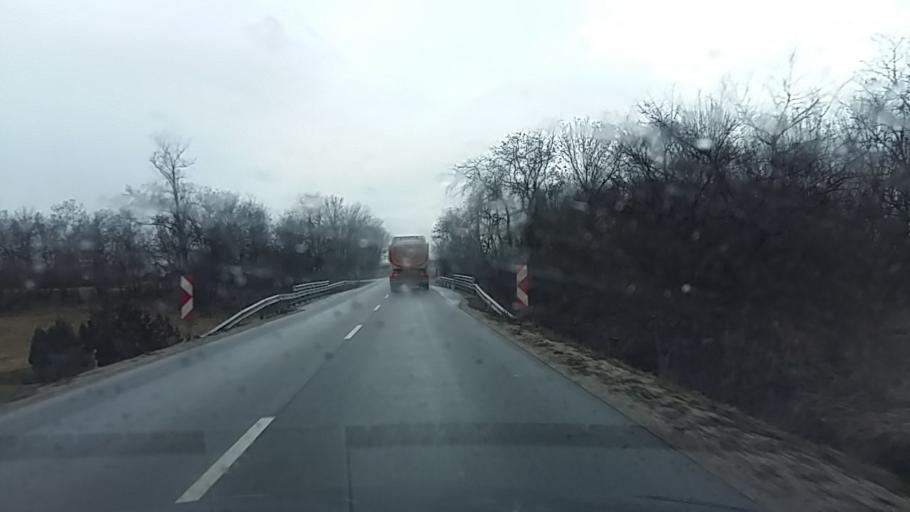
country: HU
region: Fejer
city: Pusztaszabolcs
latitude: 47.1194
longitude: 18.7922
